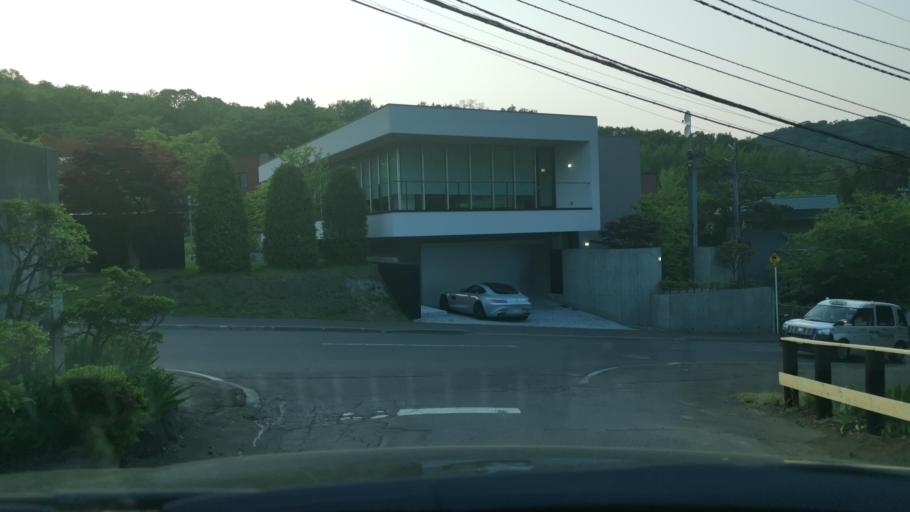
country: JP
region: Hokkaido
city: Sapporo
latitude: 43.0371
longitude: 141.3165
